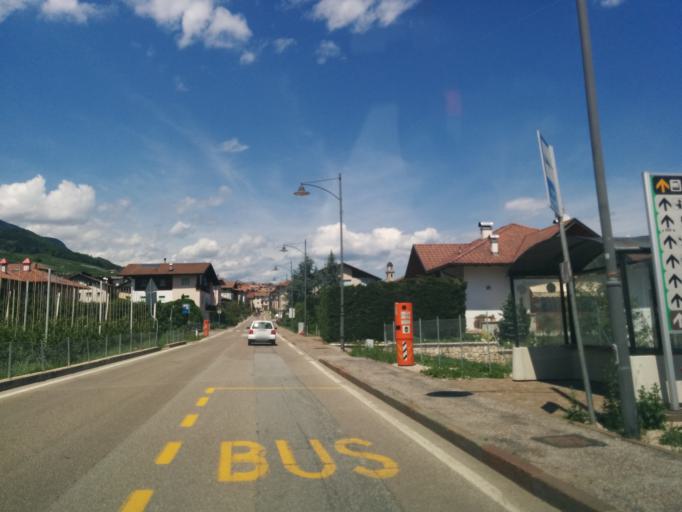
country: IT
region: Trentino-Alto Adige
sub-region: Provincia di Trento
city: Tuenno
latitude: 46.3219
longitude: 11.0219
